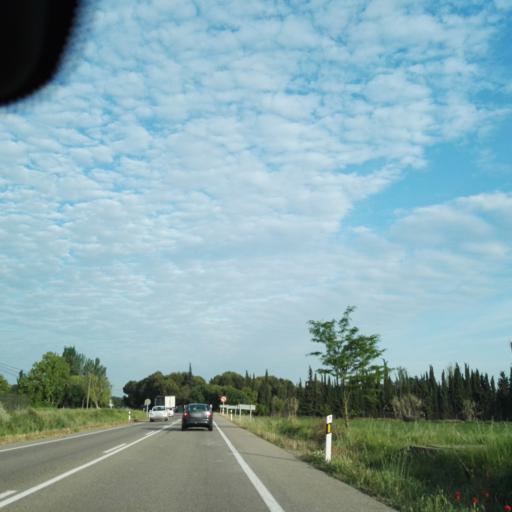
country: ES
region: Aragon
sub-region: Provincia de Zaragoza
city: Oliver-Valdefierro, Oliver, Valdefierro
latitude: 41.6635
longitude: -0.9658
